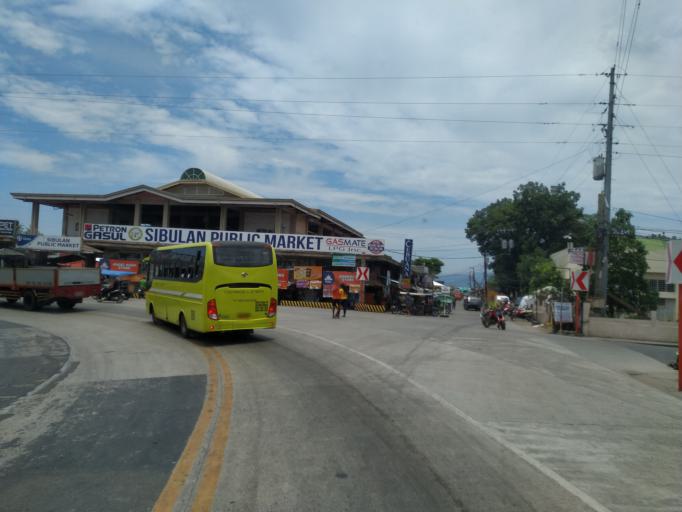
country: PH
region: Central Visayas
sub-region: Province of Negros Oriental
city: Sibulan
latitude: 9.3594
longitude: 123.2852
